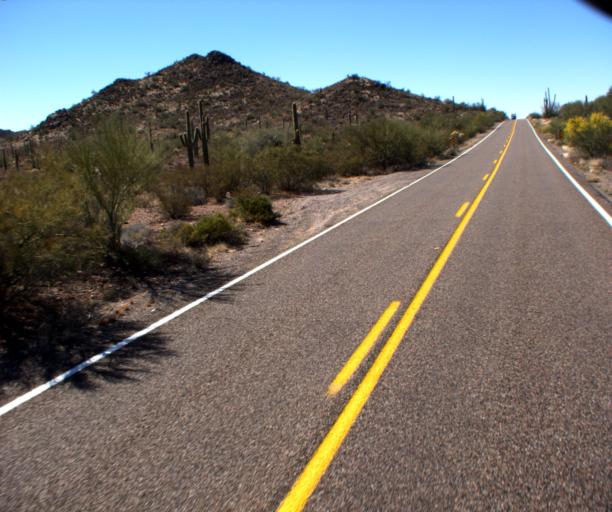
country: MX
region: Sonora
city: Sonoyta
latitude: 32.0883
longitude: -112.7760
